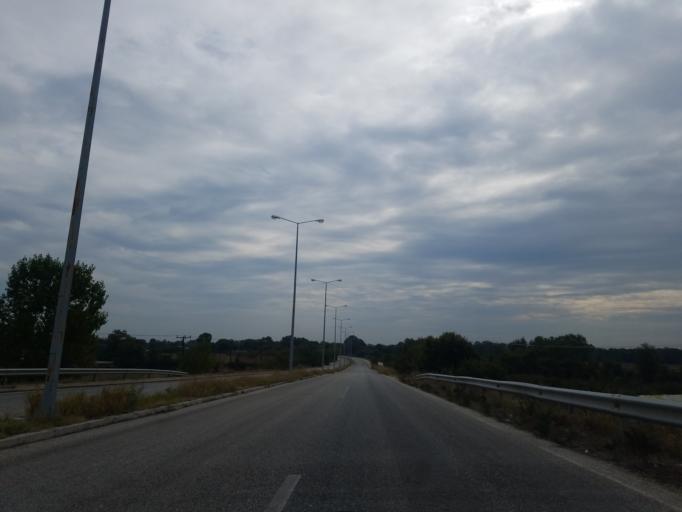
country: GR
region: Thessaly
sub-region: Trikala
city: Pyrgetos
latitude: 39.5197
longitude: 21.7589
